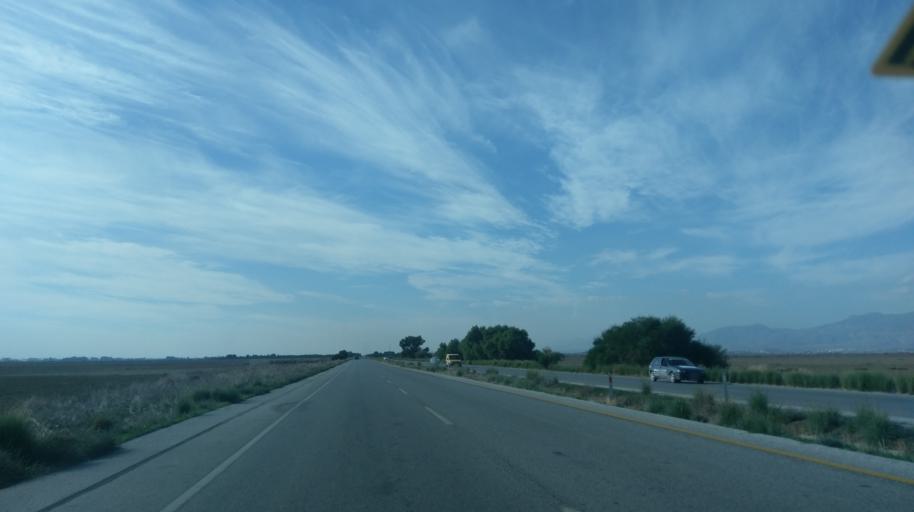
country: CY
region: Ammochostos
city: Lefkonoiko
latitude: 35.1841
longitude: 33.6806
